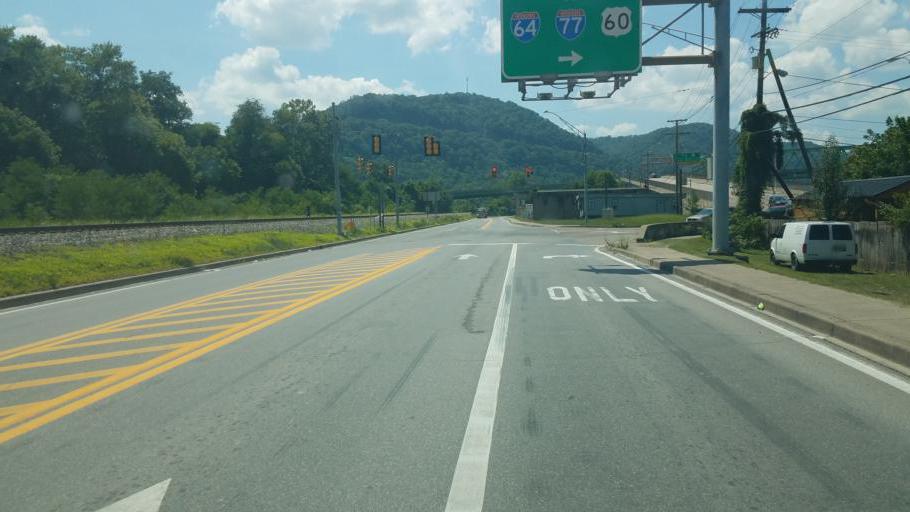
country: US
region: West Virginia
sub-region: Kanawha County
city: Chesapeake
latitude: 38.1953
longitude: -81.4925
